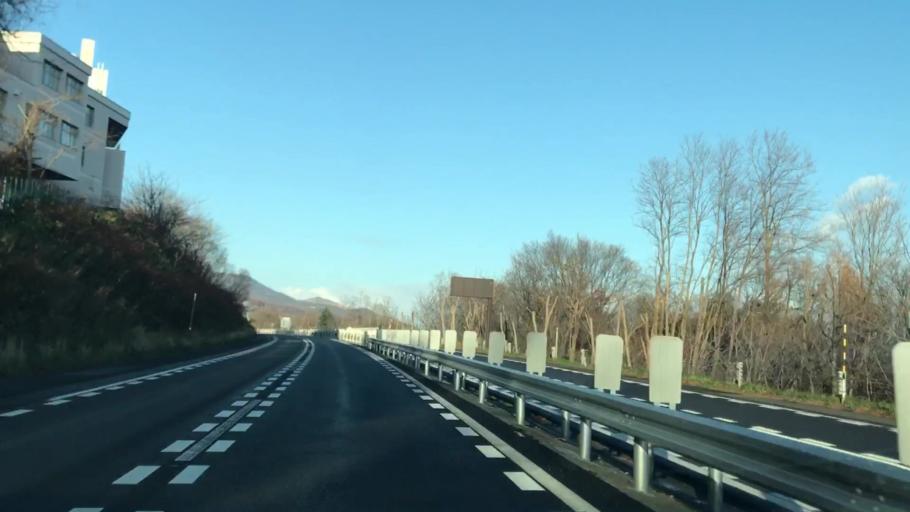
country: JP
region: Hokkaido
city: Otaru
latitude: 43.1349
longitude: 141.1692
